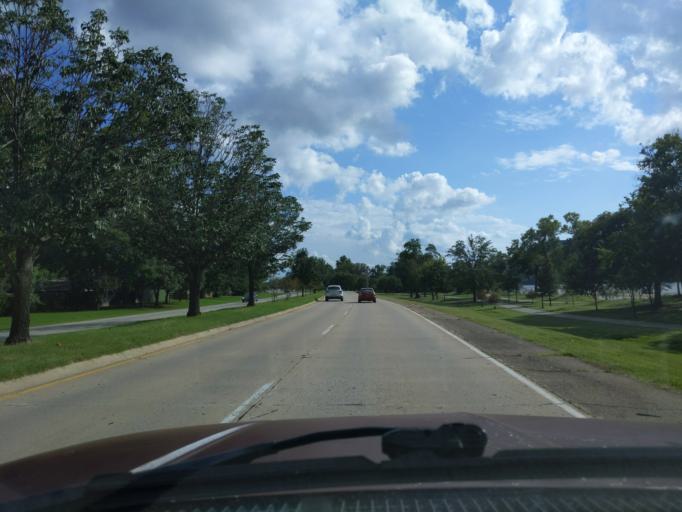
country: US
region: Oklahoma
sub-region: Tulsa County
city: Jenks
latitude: 36.0808
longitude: -95.9843
